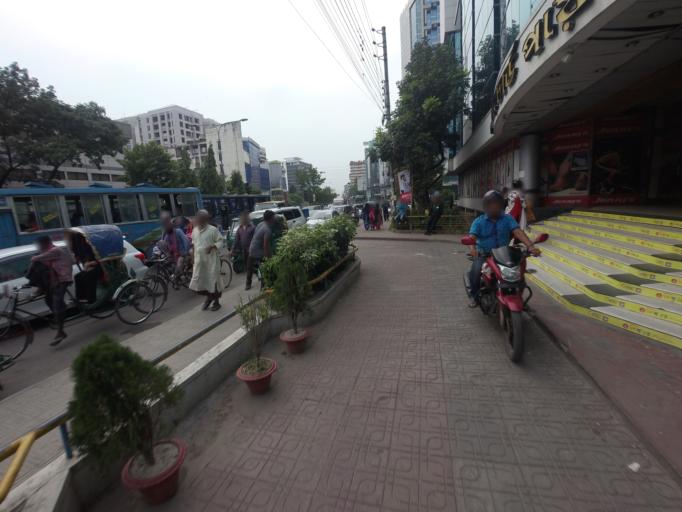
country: BD
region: Dhaka
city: Azimpur
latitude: 23.7440
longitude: 90.3824
